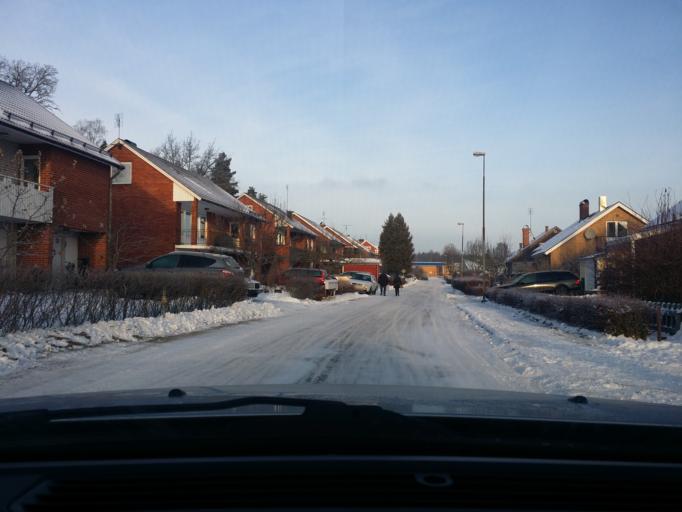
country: SE
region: OErebro
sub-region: Lindesbergs Kommun
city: Lindesberg
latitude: 59.5937
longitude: 15.2106
